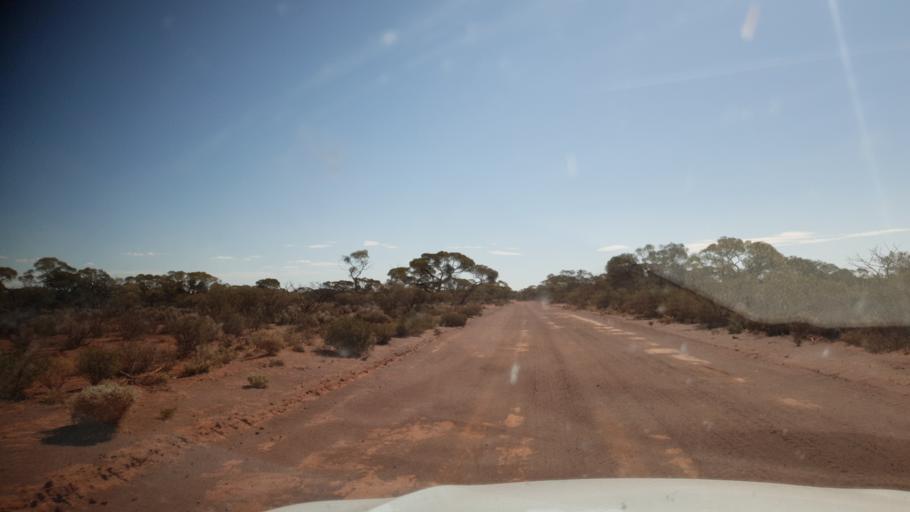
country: AU
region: South Australia
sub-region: Kimba
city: Caralue
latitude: -32.4890
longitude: 136.0642
